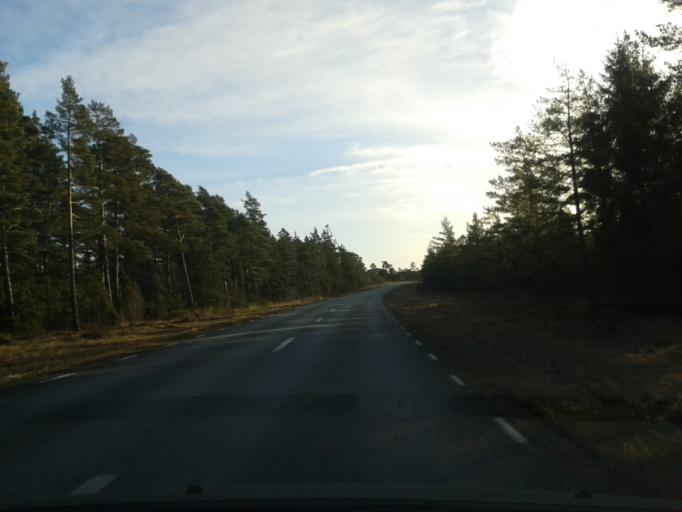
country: SE
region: Gotland
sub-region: Gotland
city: Hemse
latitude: 57.3841
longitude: 18.6602
